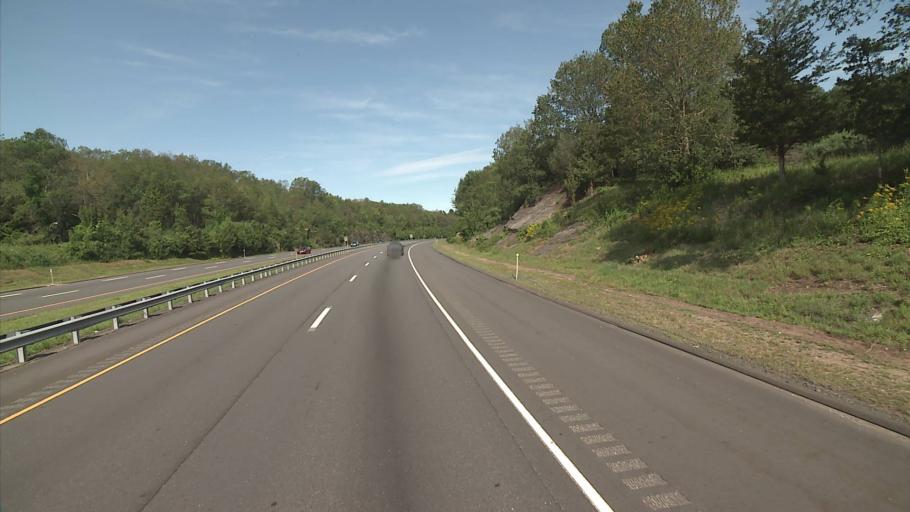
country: US
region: Connecticut
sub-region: Hartford County
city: Terramuggus
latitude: 41.5905
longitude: -72.4104
